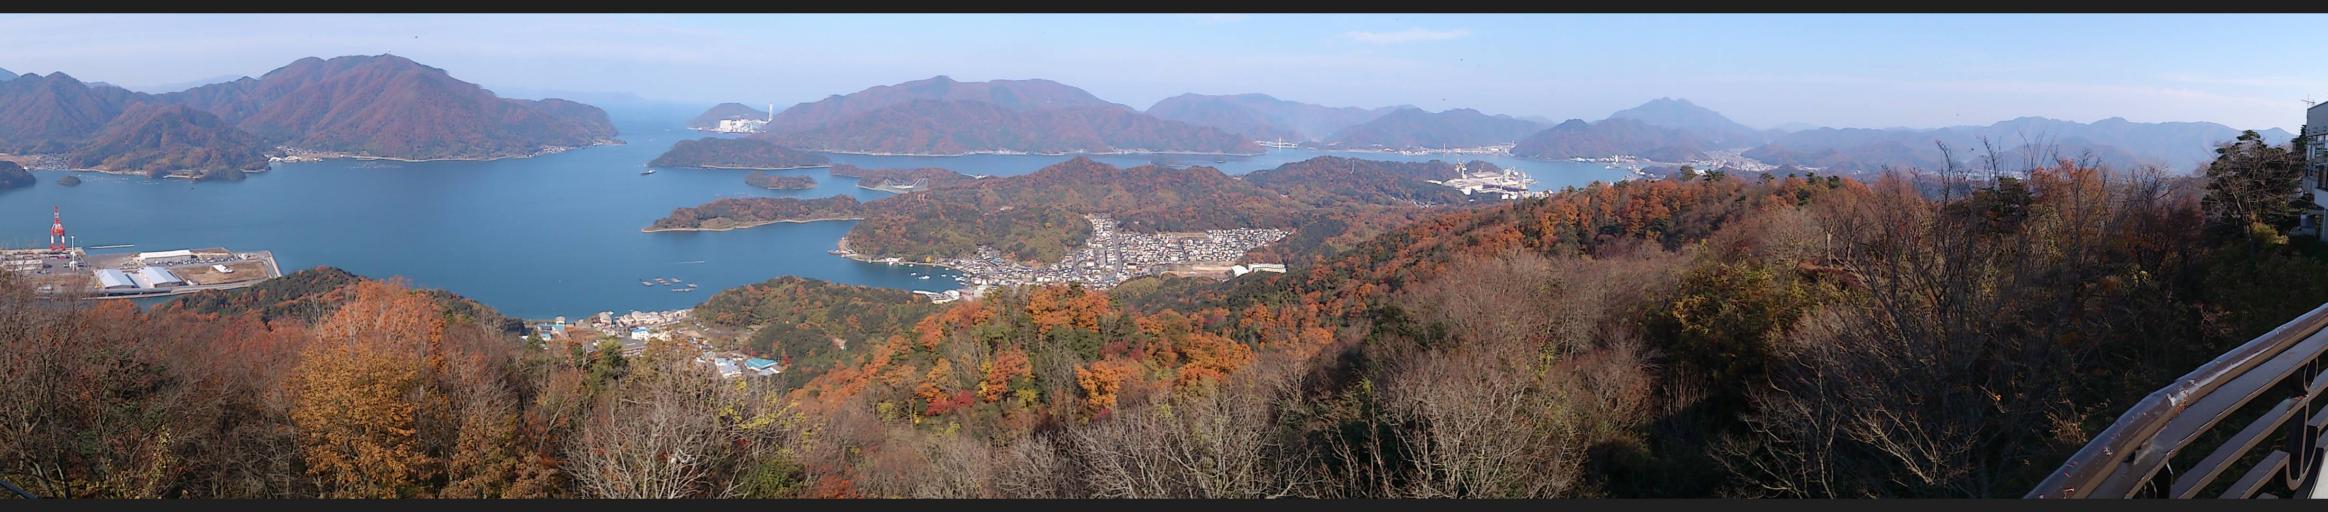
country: JP
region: Kyoto
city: Maizuru
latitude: 35.4650
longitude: 135.3434
